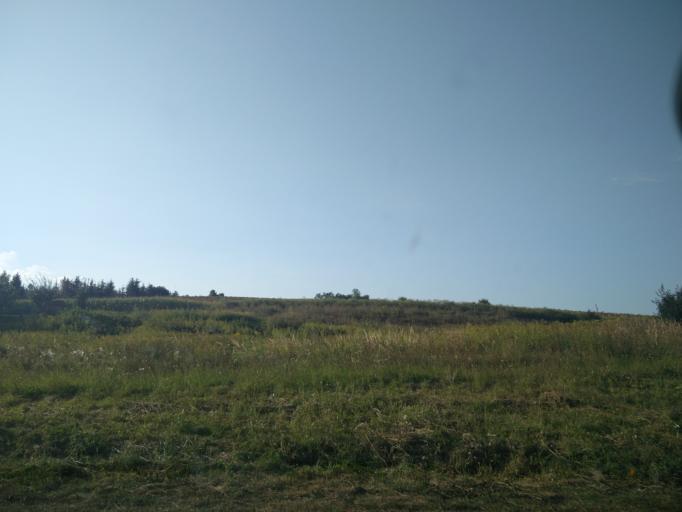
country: HU
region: Zala
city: Zalaegerszeg
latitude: 46.8346
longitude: 16.8834
